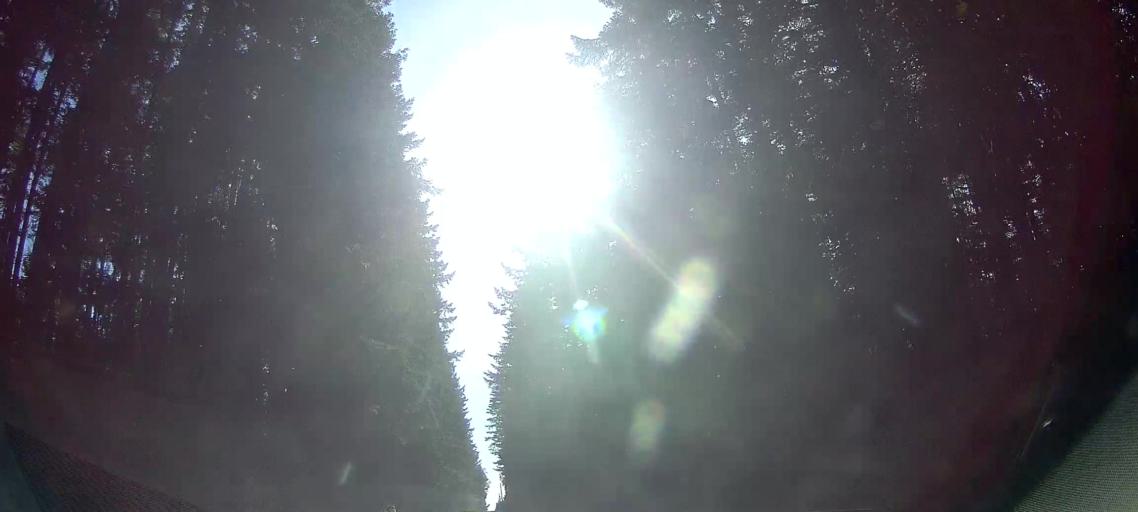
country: US
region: Washington
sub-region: Island County
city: Camano
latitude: 48.2130
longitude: -122.4561
